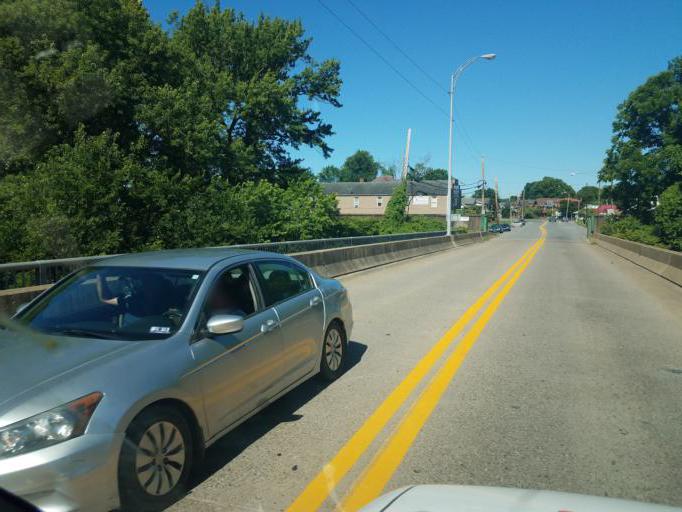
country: US
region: West Virginia
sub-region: Cabell County
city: Huntington
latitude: 38.4303
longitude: -82.3919
